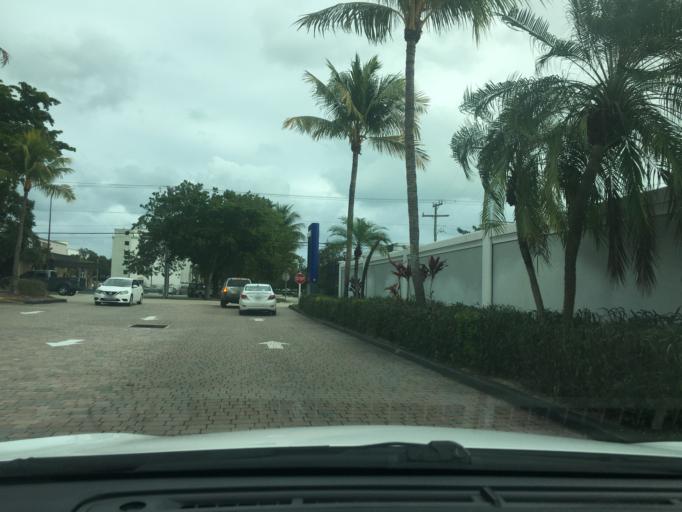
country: US
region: Florida
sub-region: Miami-Dade County
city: Biscayne Park
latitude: 25.8885
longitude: -80.1667
